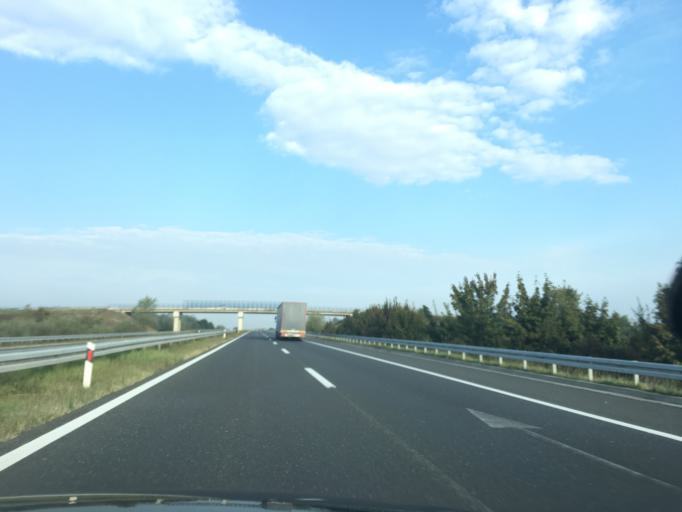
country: HR
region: Zagrebacka
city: Bestovje
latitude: 45.8062
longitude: 15.7732
